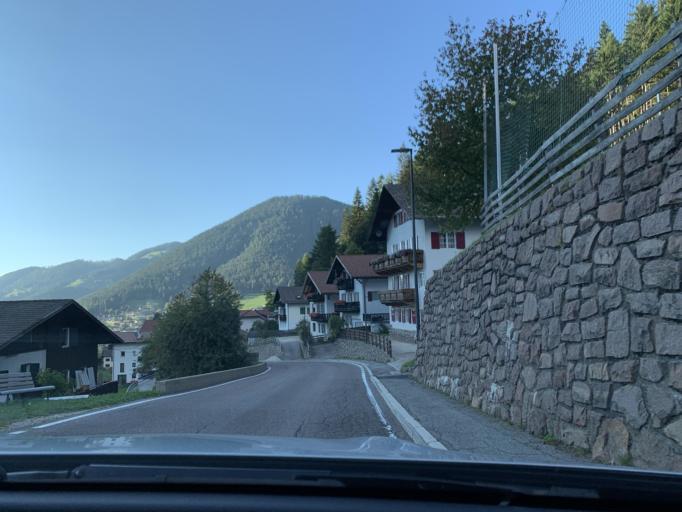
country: IT
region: Trentino-Alto Adige
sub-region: Bolzano
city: Nova Levante
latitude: 46.4247
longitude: 11.5523
